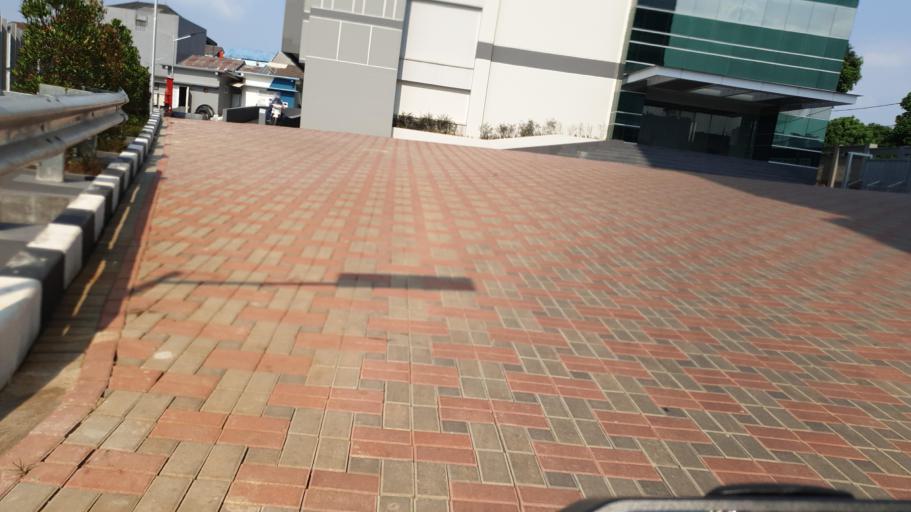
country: ID
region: West Java
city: Depok
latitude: -6.3700
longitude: 106.8399
